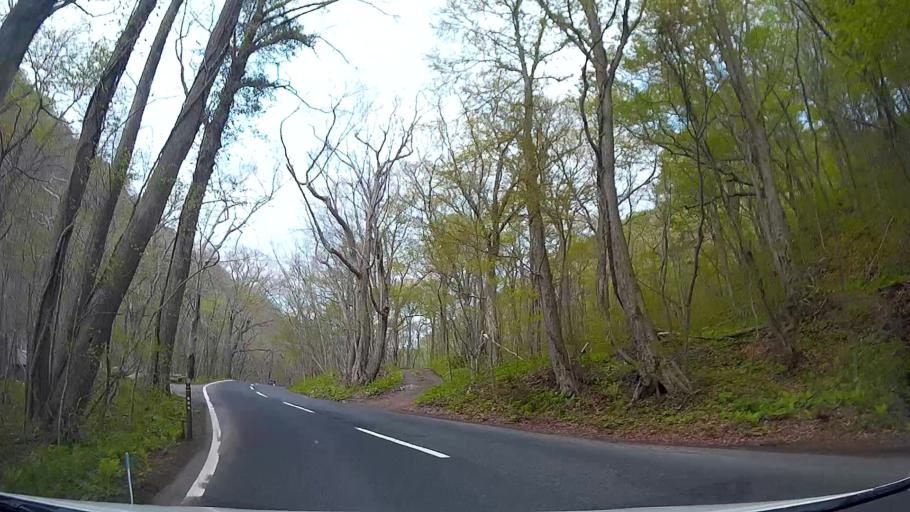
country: JP
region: Akita
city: Hanawa
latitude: 40.4795
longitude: 140.9437
